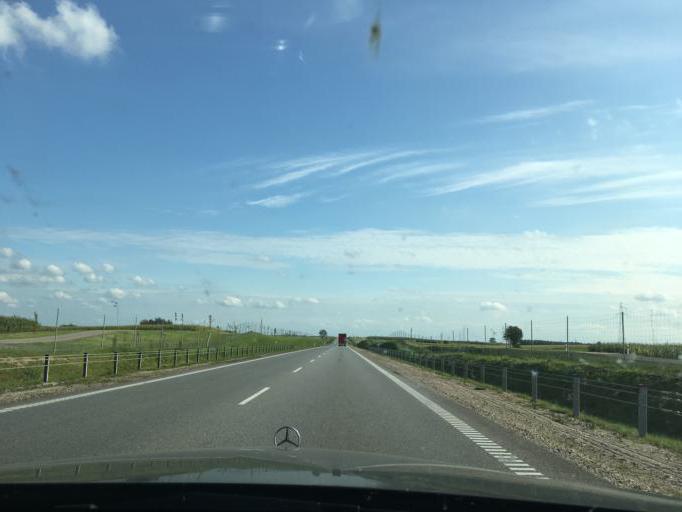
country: PL
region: Podlasie
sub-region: Powiat suwalski
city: Raczki
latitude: 53.9019
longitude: 22.8512
